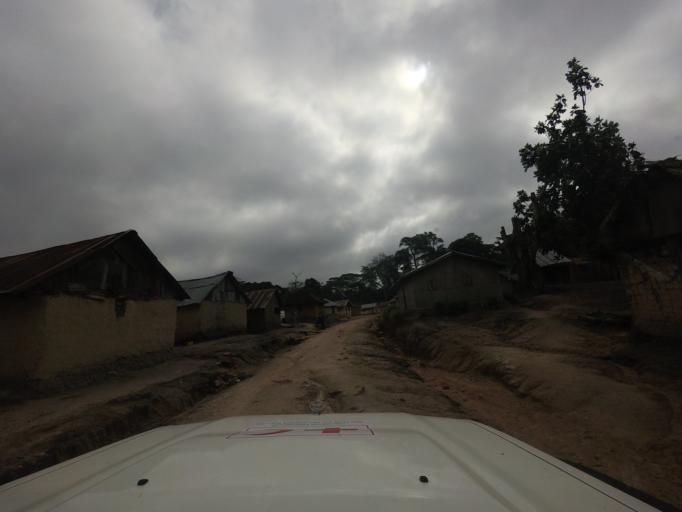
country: LR
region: Lofa
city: Voinjama
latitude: 8.4624
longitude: -9.7896
